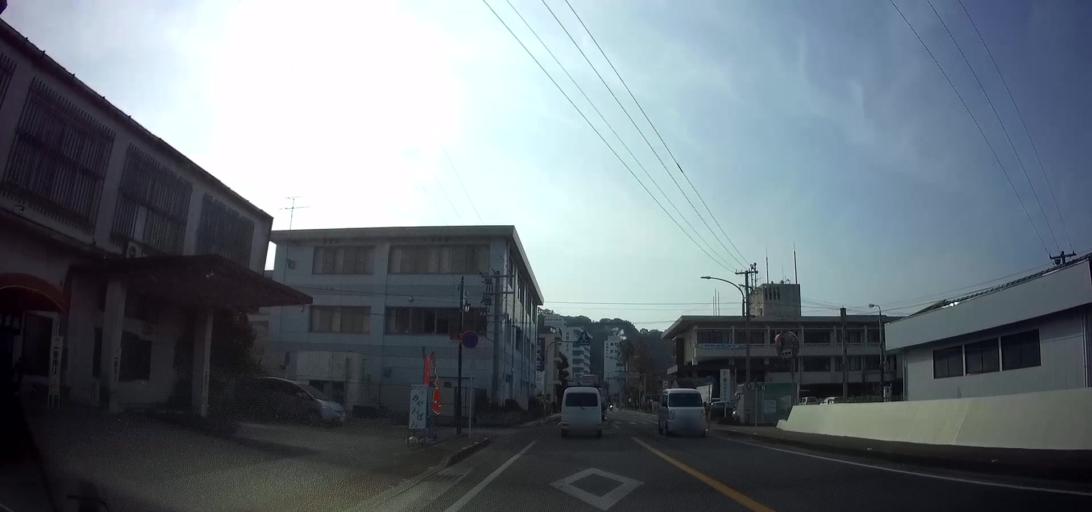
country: JP
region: Nagasaki
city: Shimabara
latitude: 32.7308
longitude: 130.2069
